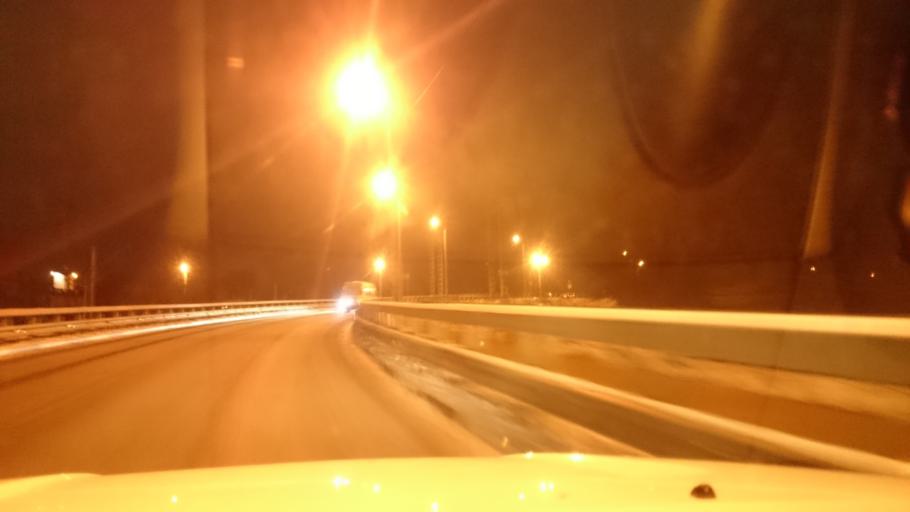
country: RU
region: Tula
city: Tula
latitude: 54.1919
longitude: 37.5724
